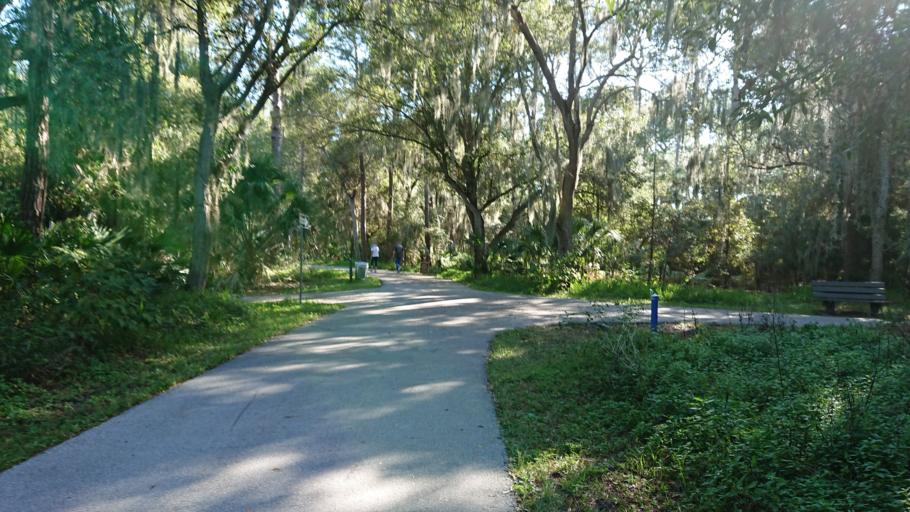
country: US
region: Florida
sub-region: Pinellas County
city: Seminole
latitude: 27.8519
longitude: -82.7762
